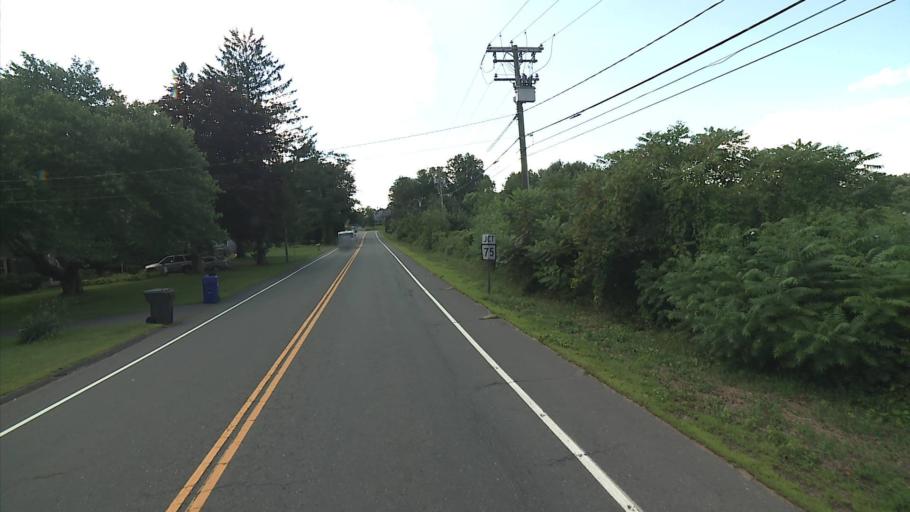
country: US
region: Connecticut
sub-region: Hartford County
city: Suffield Depot
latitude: 41.9964
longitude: -72.6428
